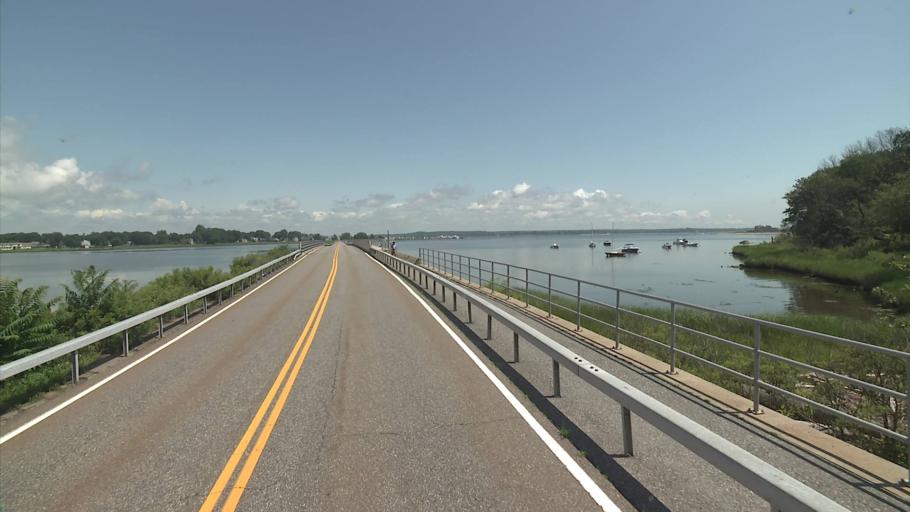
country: US
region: Connecticut
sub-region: Middlesex County
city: Old Saybrook Center
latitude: 41.2741
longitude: -72.3574
